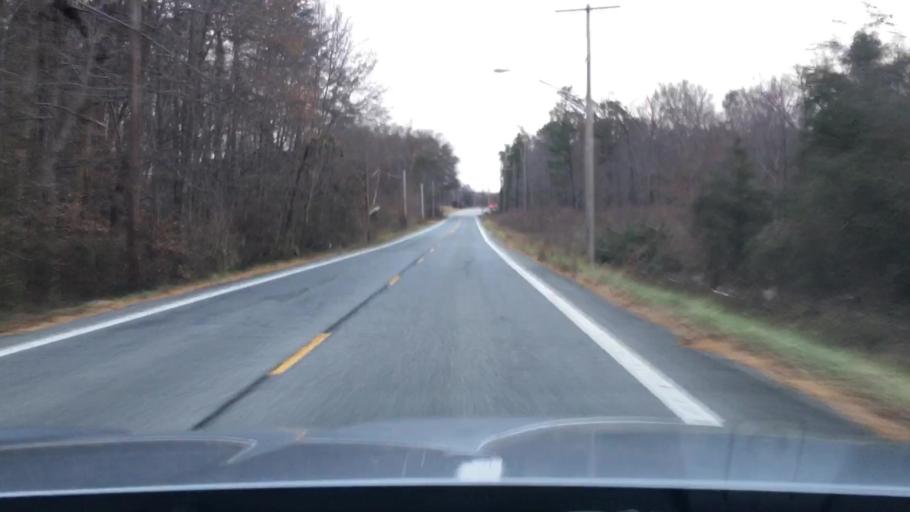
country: US
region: Maryland
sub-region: Prince George's County
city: Glenn Dale
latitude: 39.0277
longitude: -76.7854
